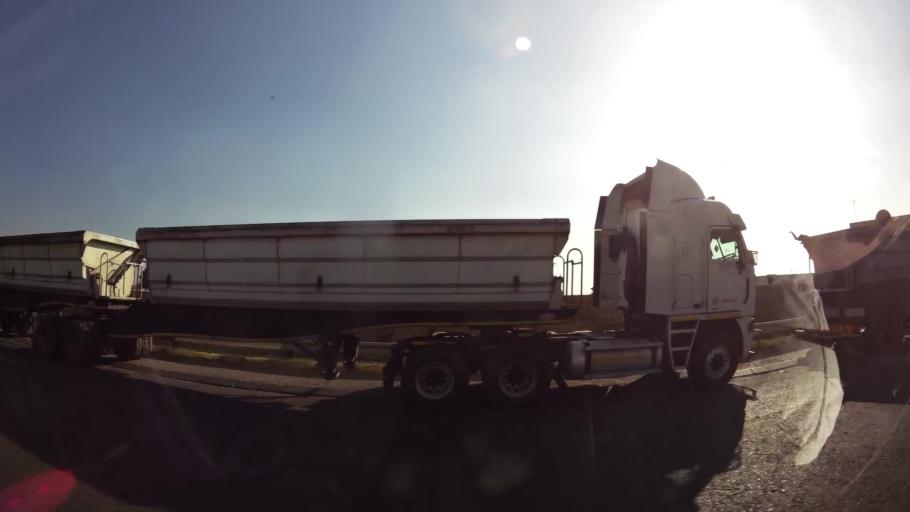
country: ZA
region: Gauteng
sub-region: West Rand District Municipality
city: Randfontein
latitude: -26.1666
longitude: 27.7121
